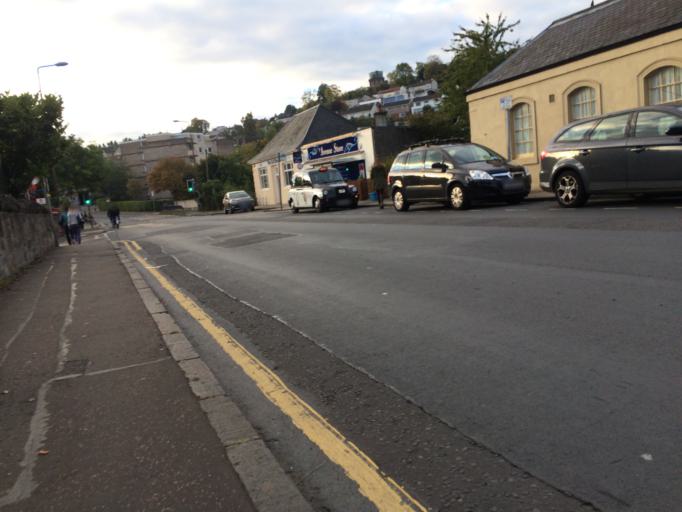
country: GB
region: Scotland
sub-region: Edinburgh
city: Edinburgh
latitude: 55.9278
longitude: -3.1877
